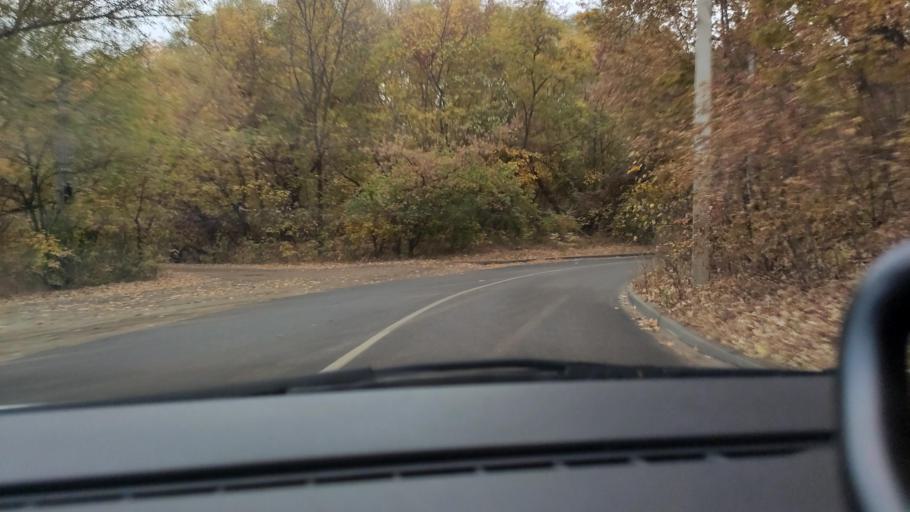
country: RU
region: Voronezj
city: Voronezh
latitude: 51.7228
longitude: 39.2369
